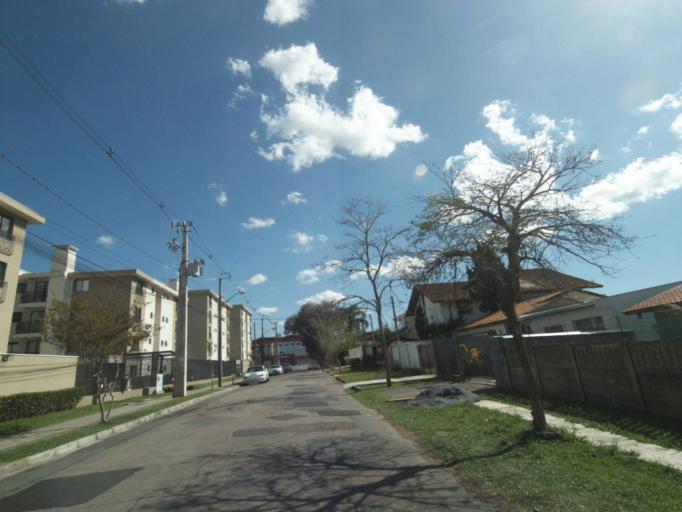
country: BR
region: Parana
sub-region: Curitiba
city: Curitiba
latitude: -25.3869
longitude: -49.2436
